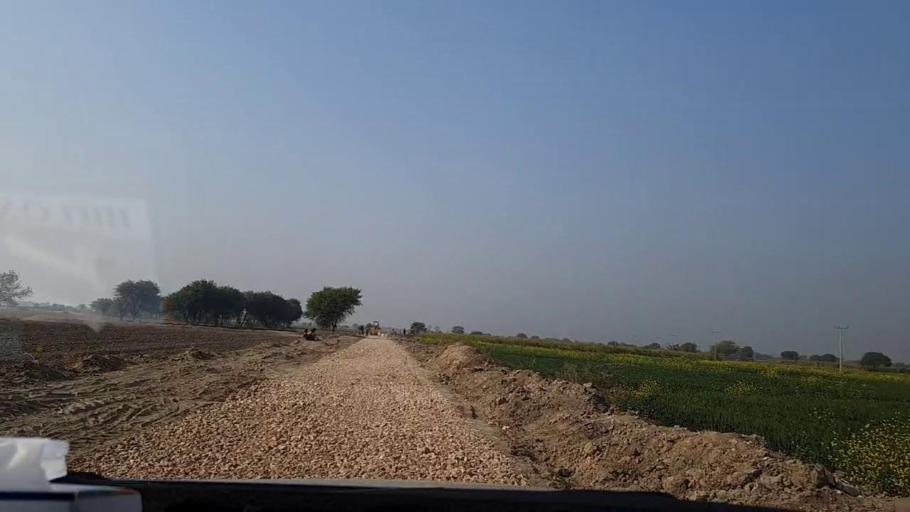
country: PK
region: Sindh
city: Tando Ghulam Ali
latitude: 25.1942
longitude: 68.8768
